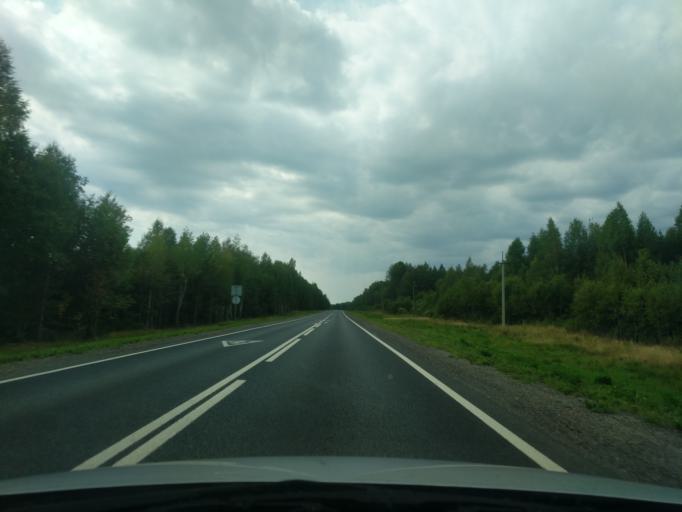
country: RU
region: Kostroma
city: Manturovo
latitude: 58.1603
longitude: 44.3936
